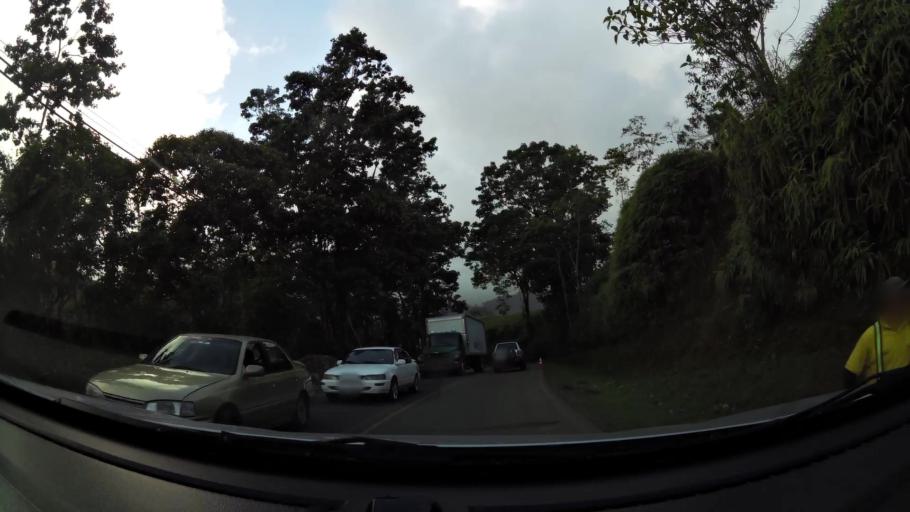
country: CR
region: Cartago
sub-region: Canton de Turrialba
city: La Suiza
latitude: 9.9663
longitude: -83.5696
